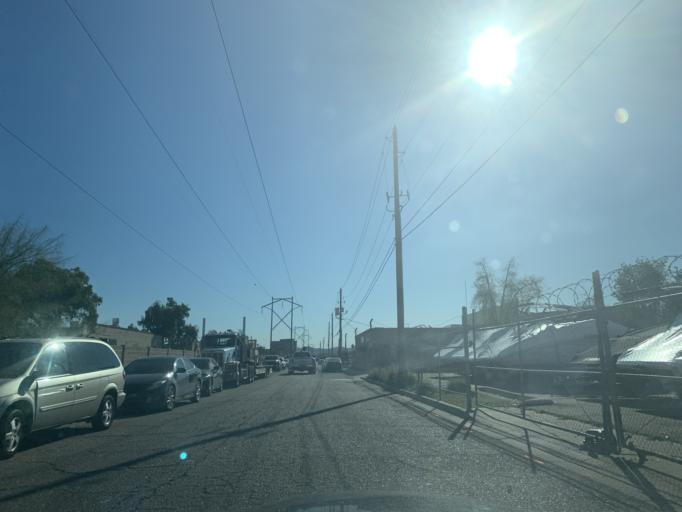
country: US
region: Arizona
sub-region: Maricopa County
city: Tempe Junction
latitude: 33.4211
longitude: -111.9824
